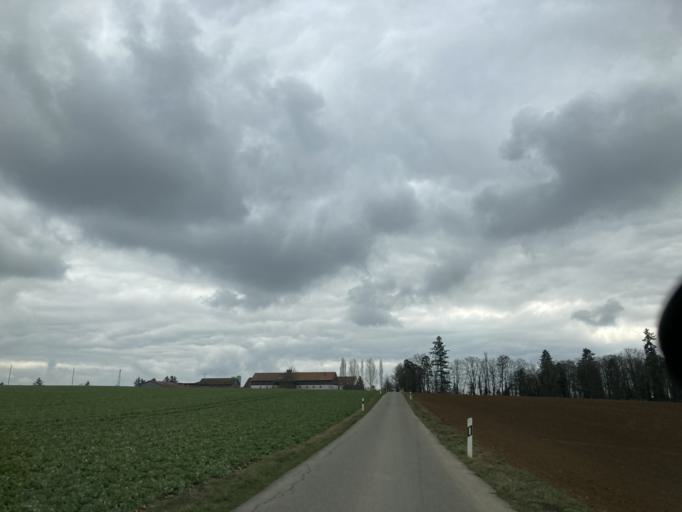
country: DE
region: Baden-Wuerttemberg
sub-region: Regierungsbezirk Stuttgart
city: Bondorf
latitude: 48.4536
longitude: 8.8194
